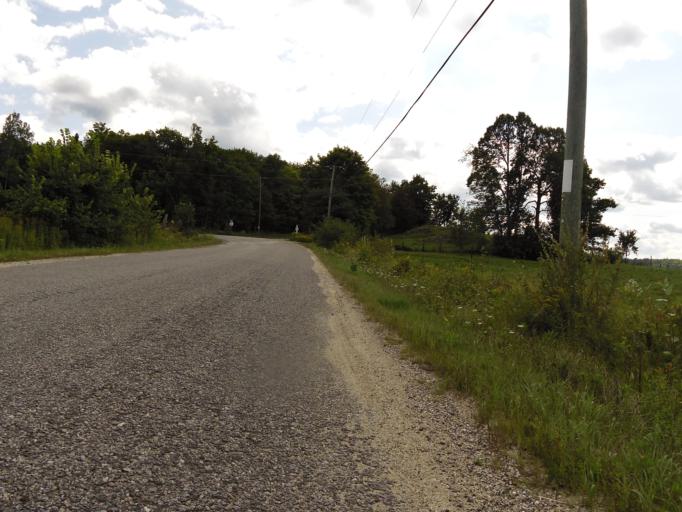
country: CA
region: Quebec
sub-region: Outaouais
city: Wakefield
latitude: 45.8044
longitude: -75.9826
